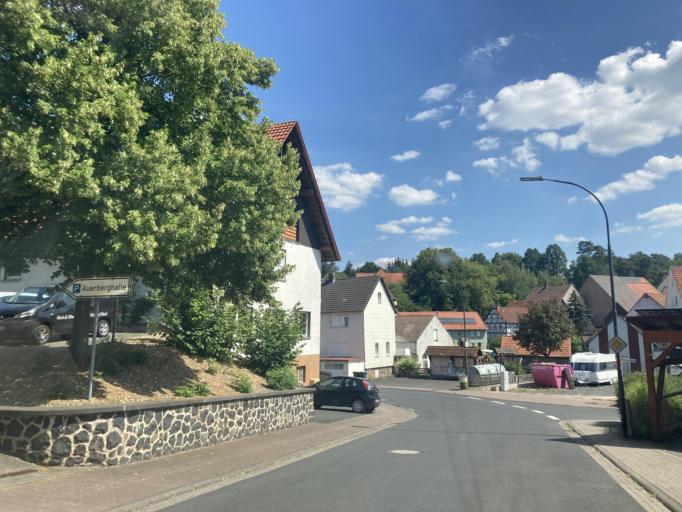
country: DE
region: Hesse
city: Grebenau
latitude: 50.7212
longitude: 9.4204
